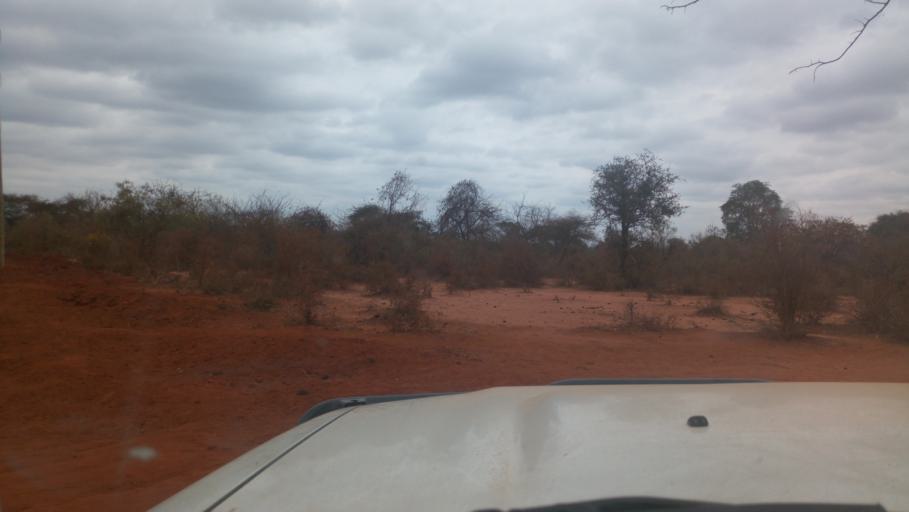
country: KE
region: Makueni
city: Wote
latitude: -1.9199
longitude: 38.0283
